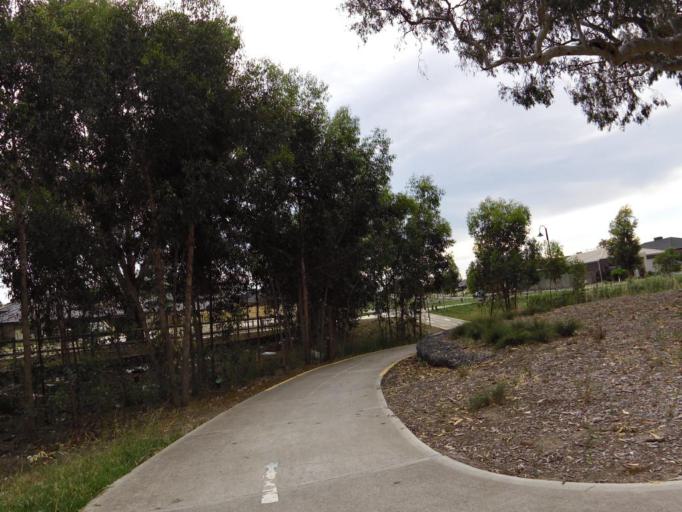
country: AU
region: Victoria
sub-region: Whittlesea
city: Mernda
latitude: -37.6328
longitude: 145.0840
